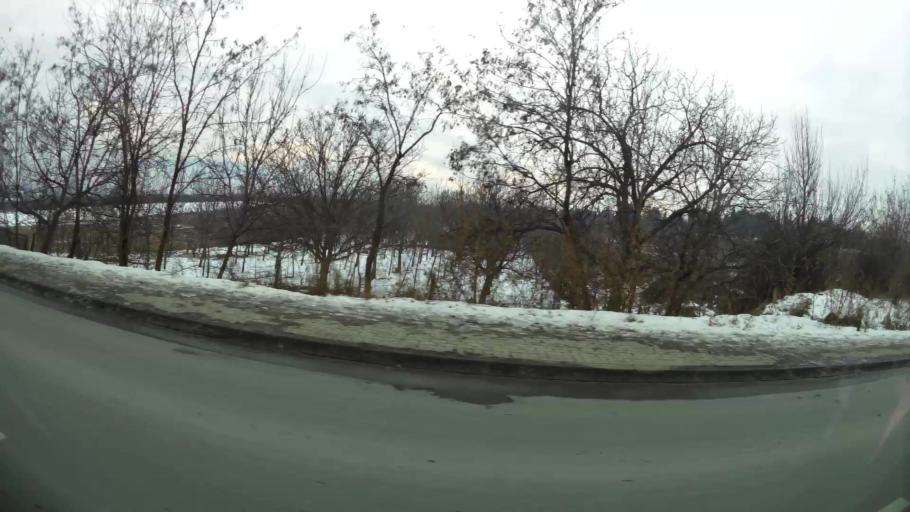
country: MK
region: Butel
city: Butel
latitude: 42.0393
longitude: 21.4400
